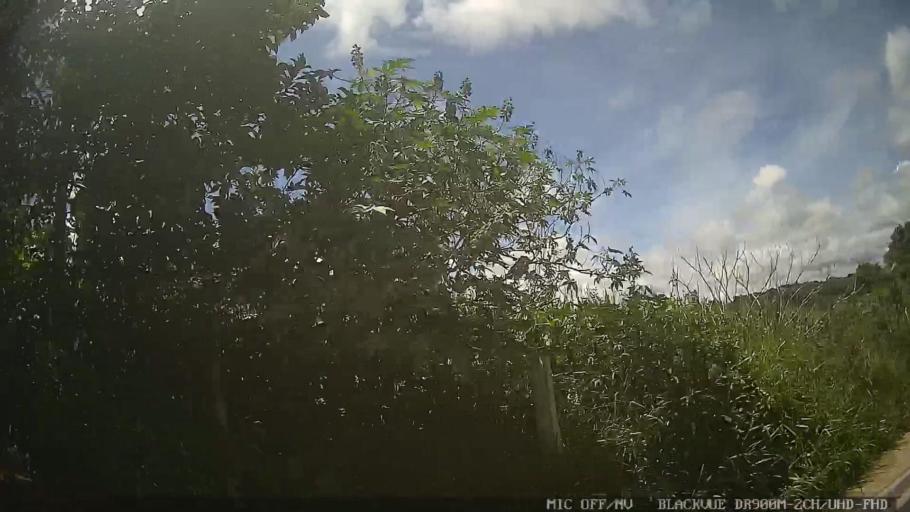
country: BR
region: Sao Paulo
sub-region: Amparo
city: Amparo
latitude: -22.8216
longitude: -46.6952
